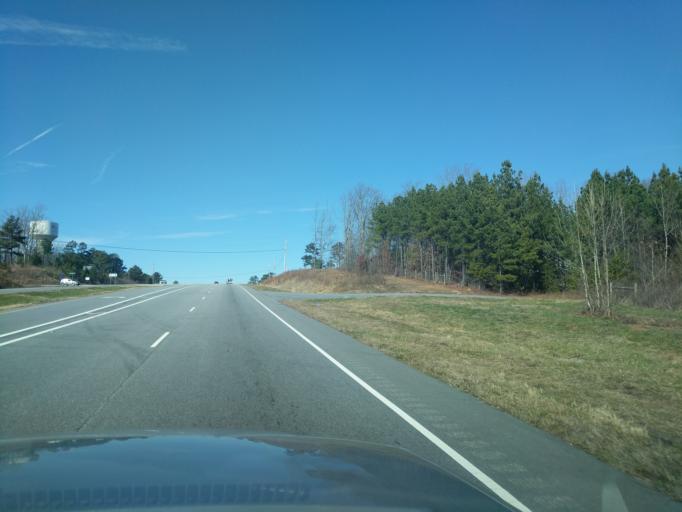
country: US
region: North Carolina
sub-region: Rutherford County
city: Forest City
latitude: 35.2551
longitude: -81.8777
